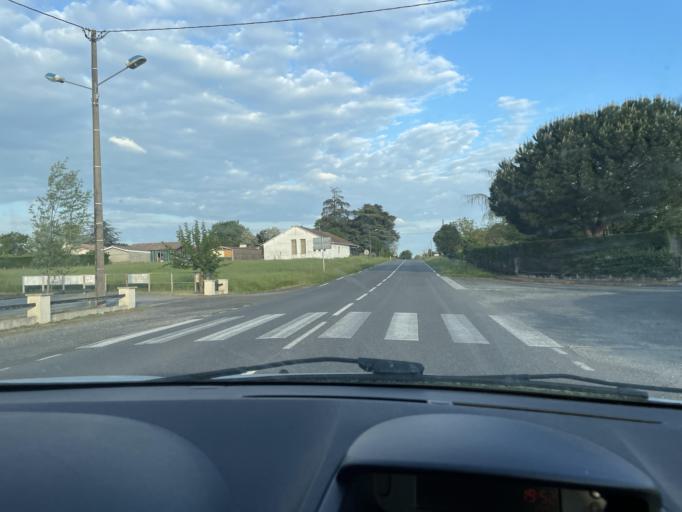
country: FR
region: Aquitaine
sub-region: Departement de la Gironde
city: Grignols
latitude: 44.3850
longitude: -0.0404
